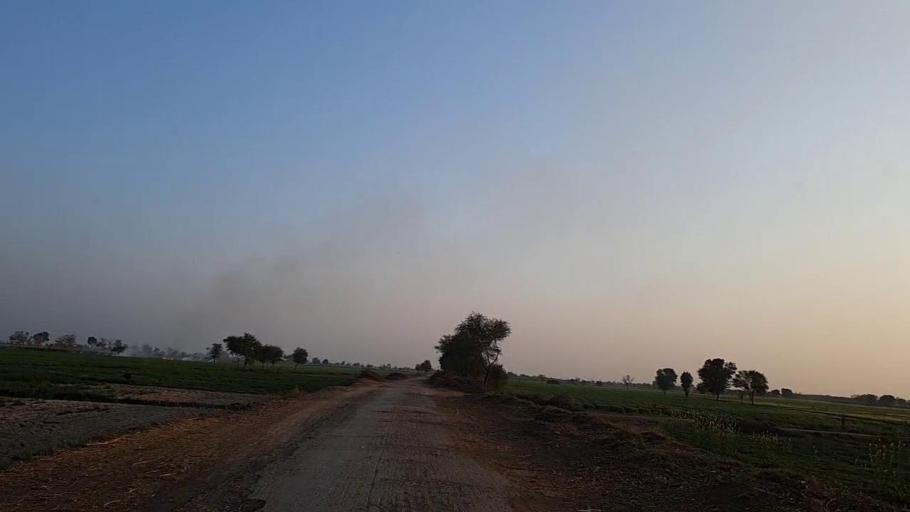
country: PK
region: Sindh
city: Shahdadpur
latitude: 25.9531
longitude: 68.5014
